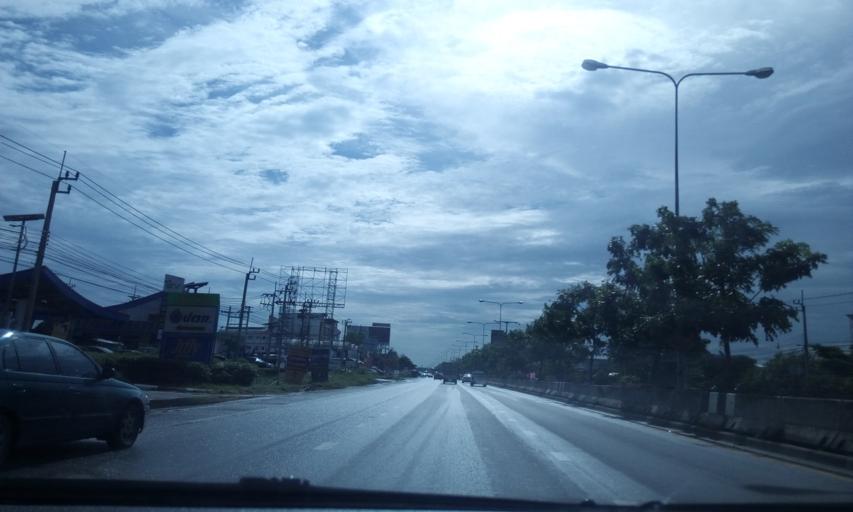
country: TH
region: Nonthaburi
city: Pak Kret
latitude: 13.9233
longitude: 100.4748
